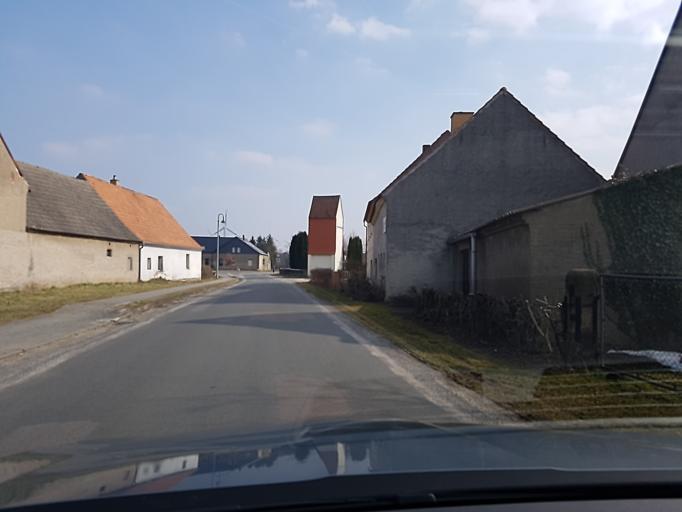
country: DE
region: Brandenburg
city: Falkenberg
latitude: 51.5292
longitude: 13.2961
